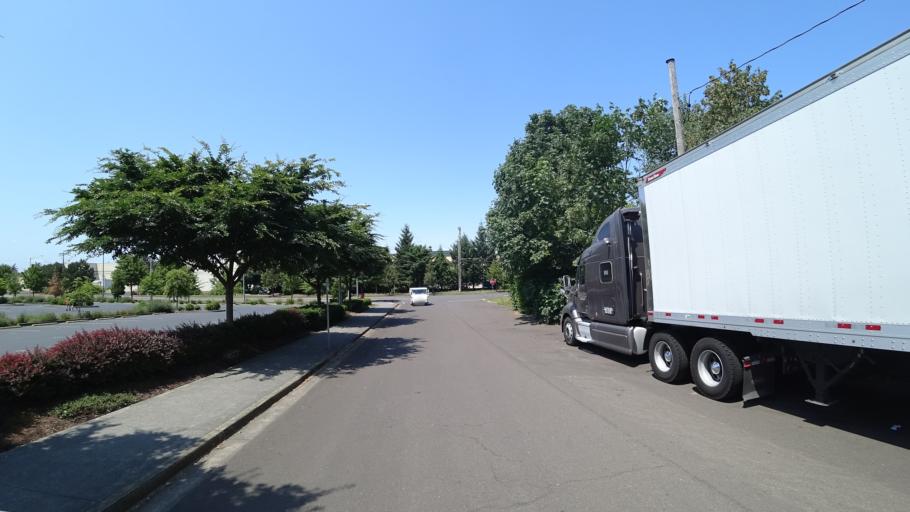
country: US
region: Oregon
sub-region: Multnomah County
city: Lents
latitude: 45.4540
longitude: -122.5751
